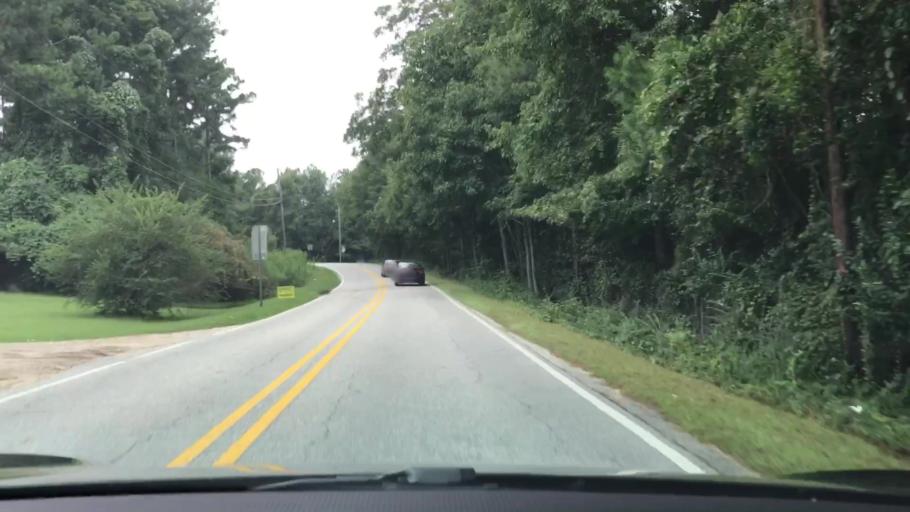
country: US
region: Alabama
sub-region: Lee County
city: Auburn
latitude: 32.6186
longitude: -85.4446
